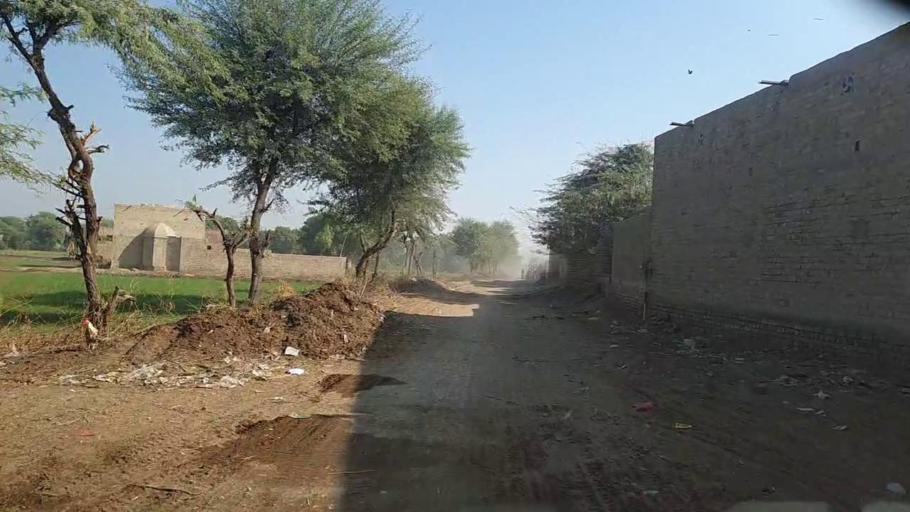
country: PK
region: Sindh
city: Darya Khan Marri
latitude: 26.6733
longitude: 68.3225
